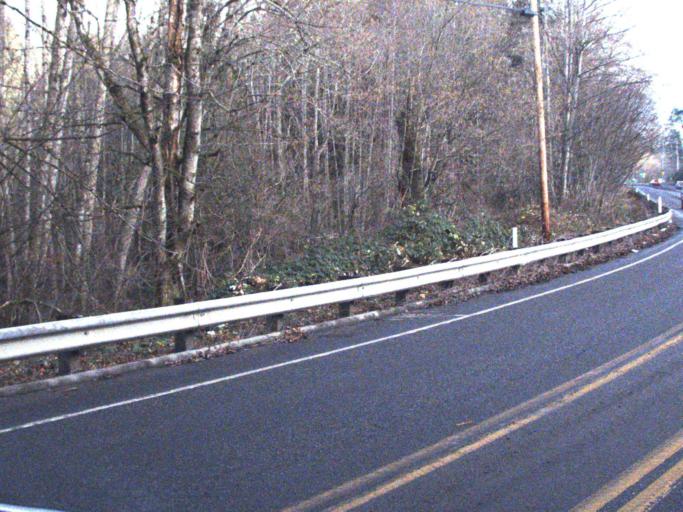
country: US
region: Washington
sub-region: Skagit County
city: Big Lake
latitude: 48.4299
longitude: -122.2682
